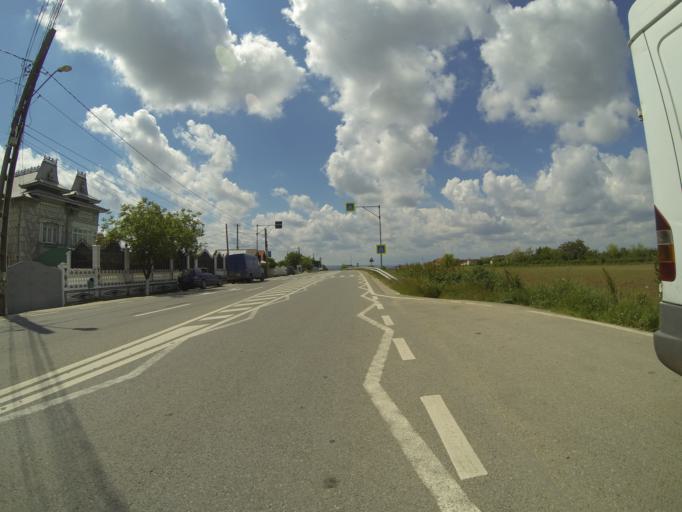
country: RO
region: Dolj
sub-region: Comuna Carcea
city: Carcea
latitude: 44.2643
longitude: 23.8996
